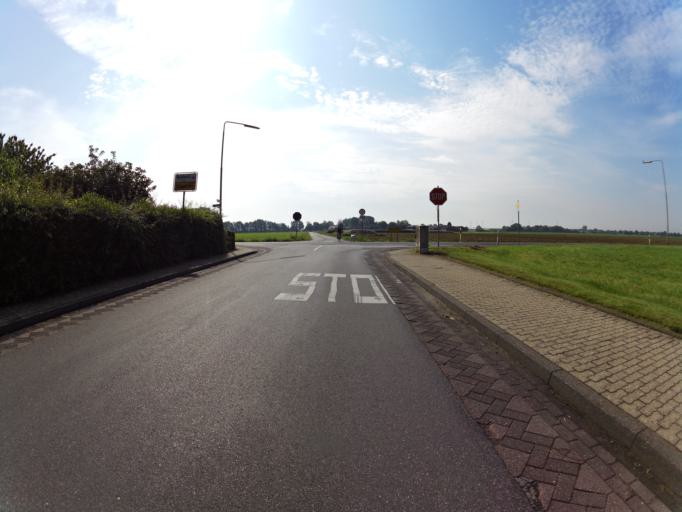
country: DE
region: North Rhine-Westphalia
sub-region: Regierungsbezirk Koln
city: Waldfeucht
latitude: 51.0721
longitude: 5.9997
